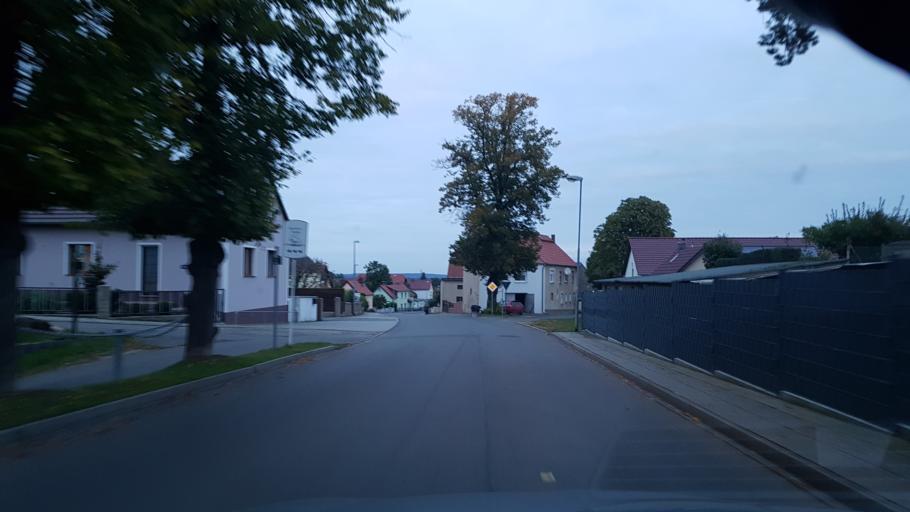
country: DE
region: Brandenburg
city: Hirschfeld
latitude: 51.3823
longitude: 13.6144
